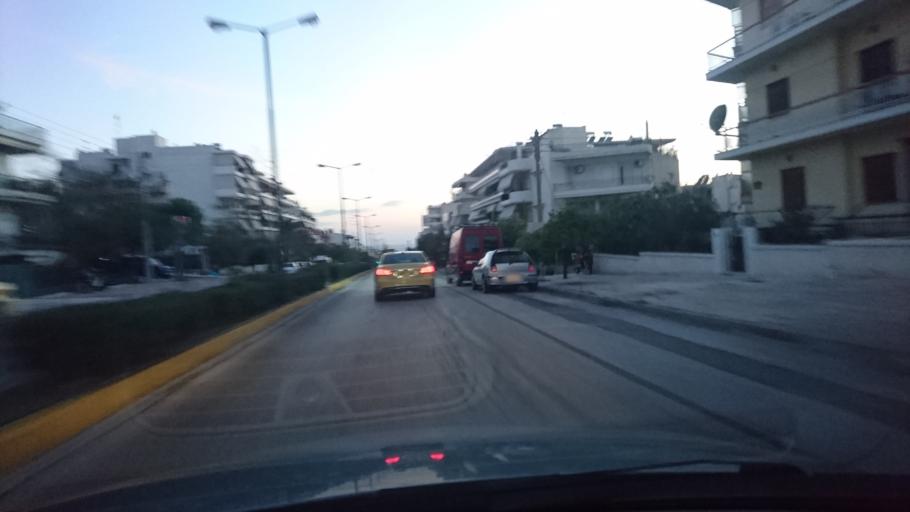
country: GR
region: Attica
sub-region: Nomarchia Athinas
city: Argyroupoli
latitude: 37.9203
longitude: 23.7490
